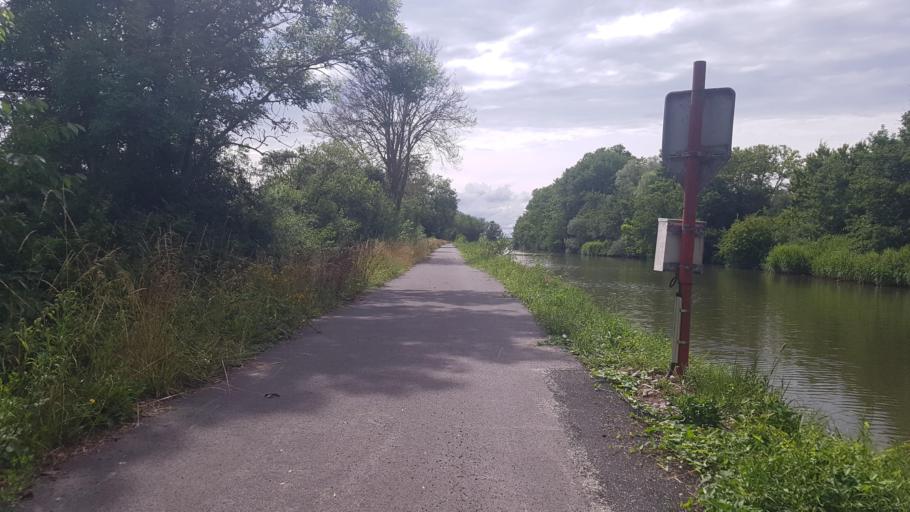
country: FR
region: Lorraine
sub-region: Departement de la Moselle
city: Dieuze
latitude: 48.6804
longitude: 6.7867
